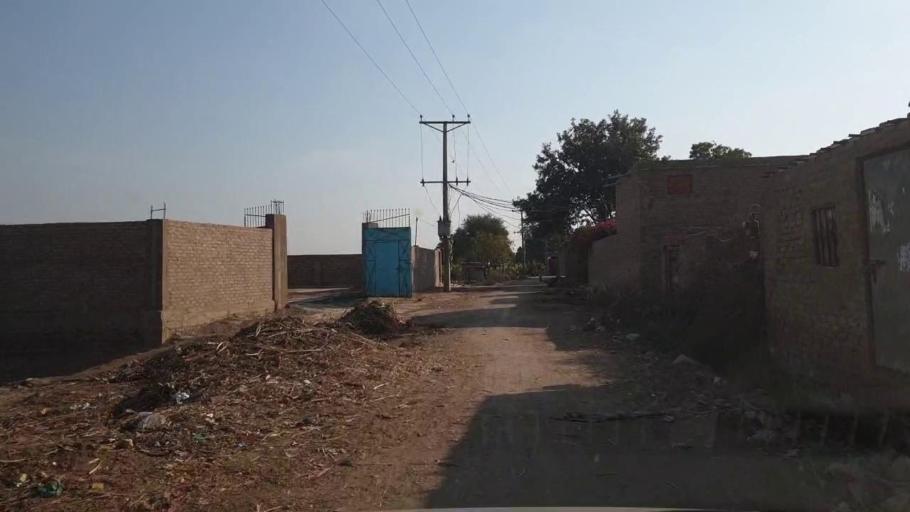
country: PK
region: Sindh
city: Chambar
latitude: 25.3214
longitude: 68.7583
